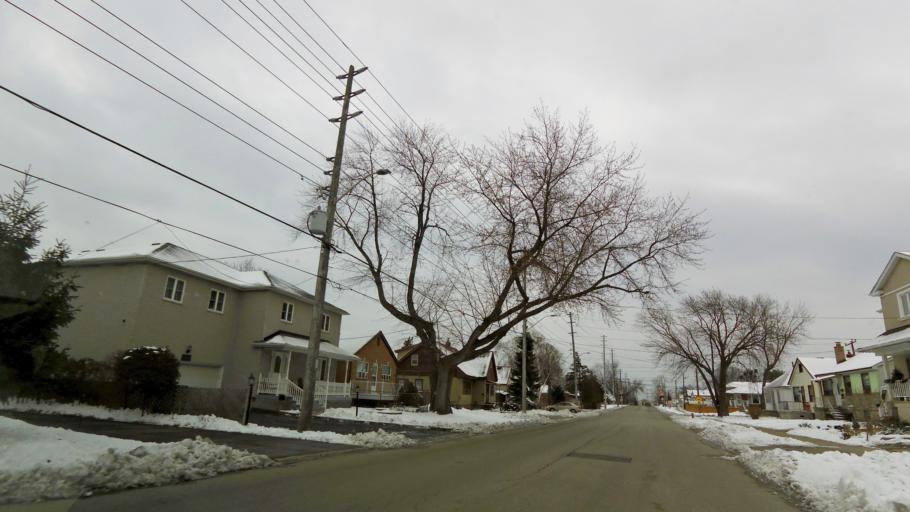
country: CA
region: Ontario
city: Etobicoke
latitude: 43.5801
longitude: -79.5632
